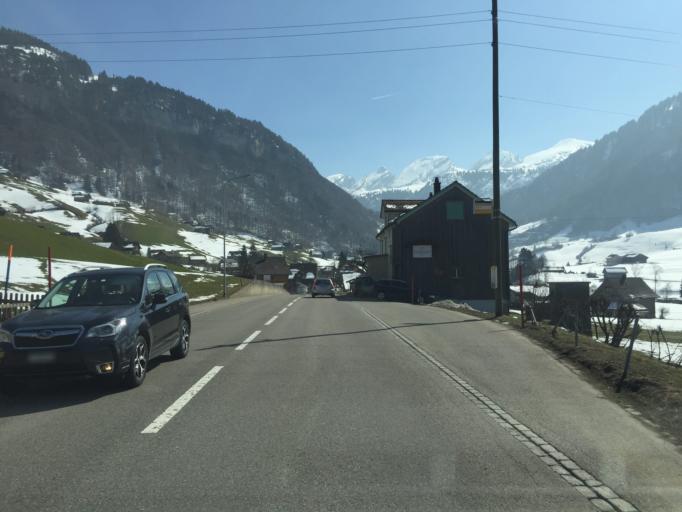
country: CH
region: Saint Gallen
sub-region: Wahlkreis Toggenburg
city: Krummenau
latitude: 47.2048
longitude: 9.2216
